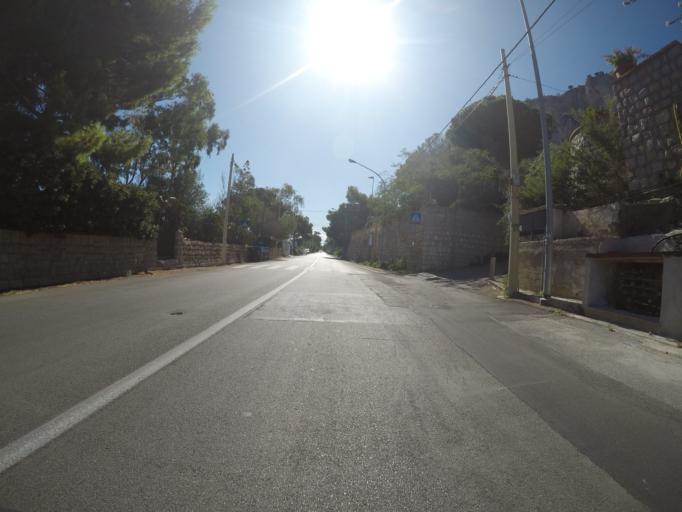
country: IT
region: Sicily
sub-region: Palermo
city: Palermo
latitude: 38.1869
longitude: 13.3606
